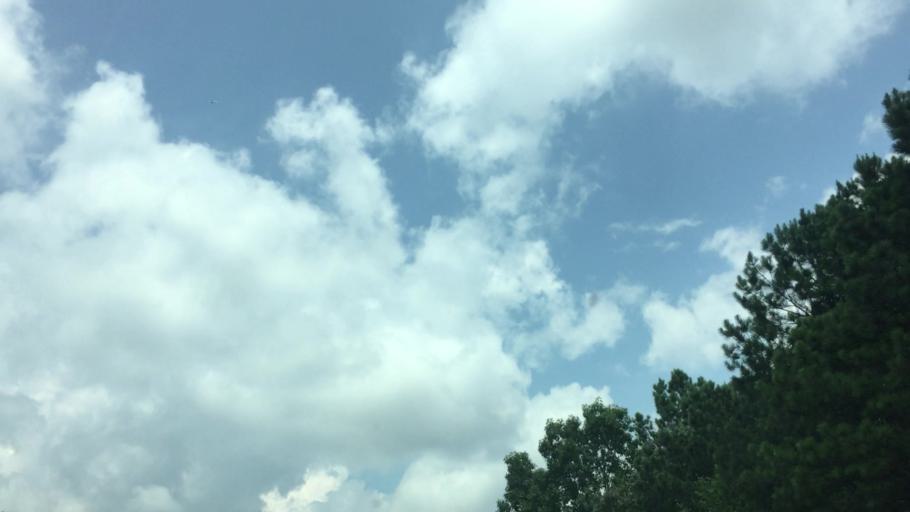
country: US
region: Georgia
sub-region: Fulton County
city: Chattahoochee Hills
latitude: 33.6104
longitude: -84.8271
